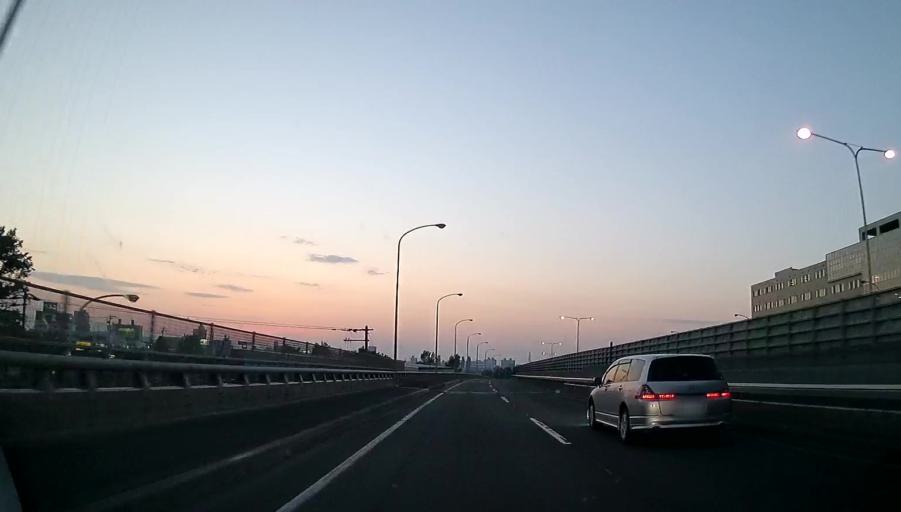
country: JP
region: Hokkaido
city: Sapporo
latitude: 43.0279
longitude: 141.4478
